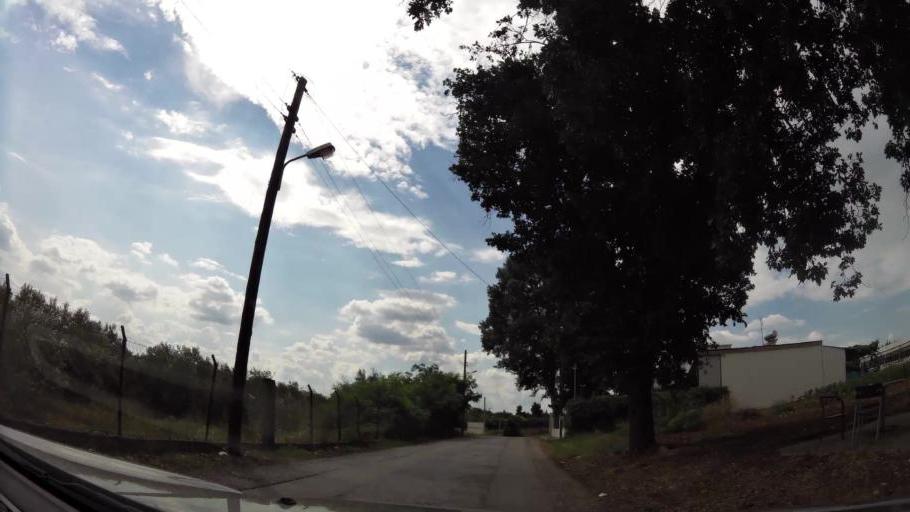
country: GR
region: Central Macedonia
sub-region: Nomos Pierias
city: Makrygialos
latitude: 40.4164
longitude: 22.5953
